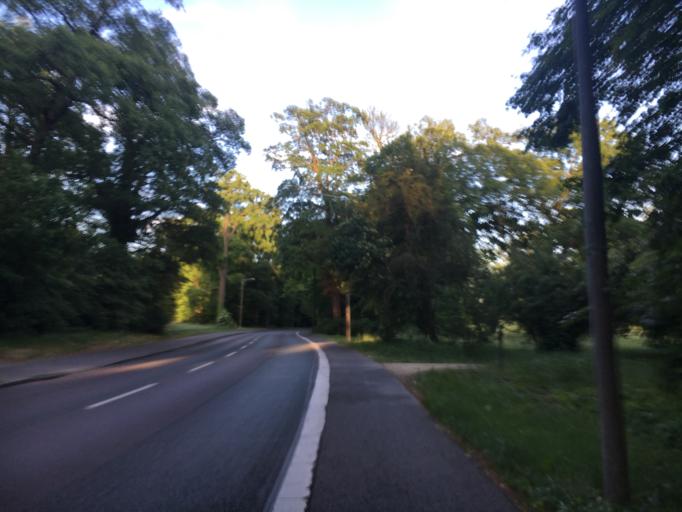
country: DE
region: Brandenburg
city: Potsdam
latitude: 52.4061
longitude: 13.0372
